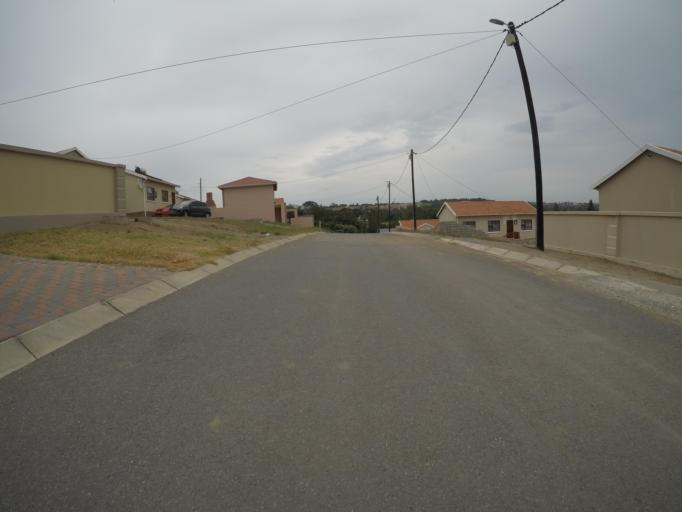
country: ZA
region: Eastern Cape
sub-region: Buffalo City Metropolitan Municipality
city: East London
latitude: -33.0020
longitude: 27.8543
